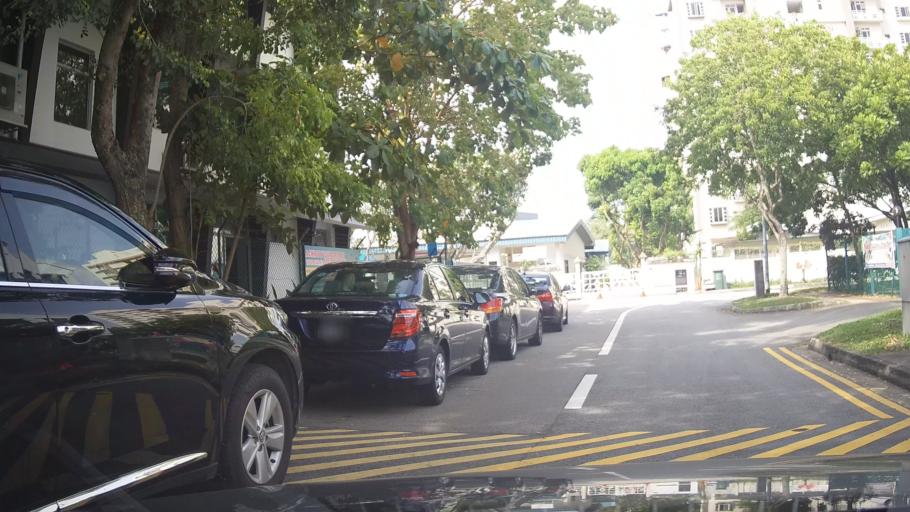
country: SG
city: Singapore
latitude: 1.3093
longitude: 103.8809
